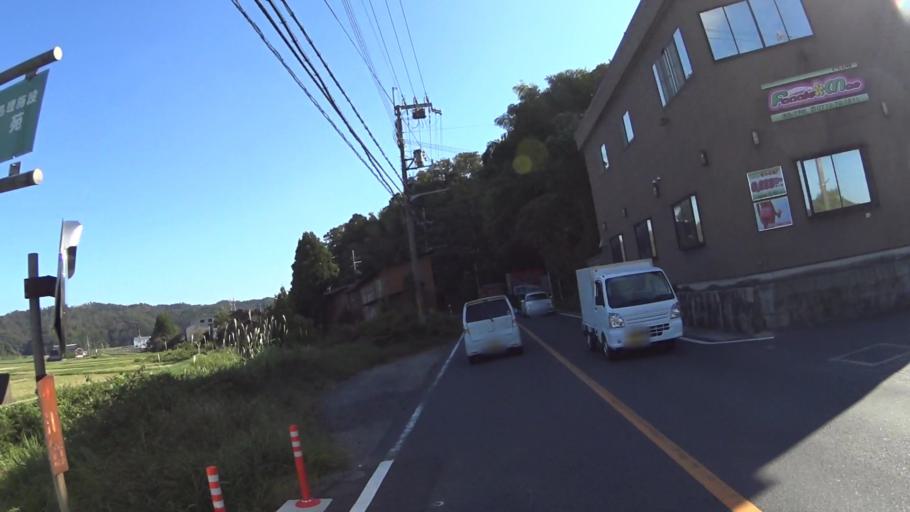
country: JP
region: Kyoto
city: Miyazu
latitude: 35.6651
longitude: 135.0285
